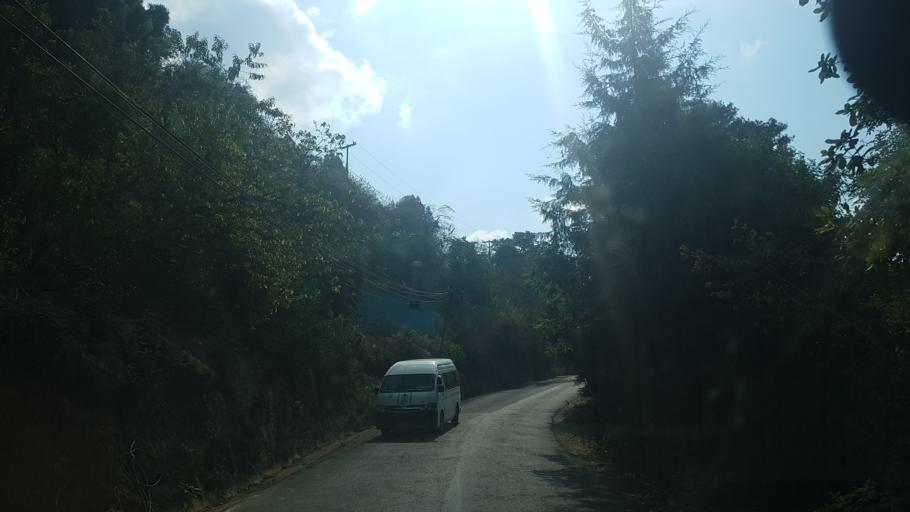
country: MX
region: Puebla
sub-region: Tochimilco
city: San Antonio Alpanocan
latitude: 18.8768
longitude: -98.7024
